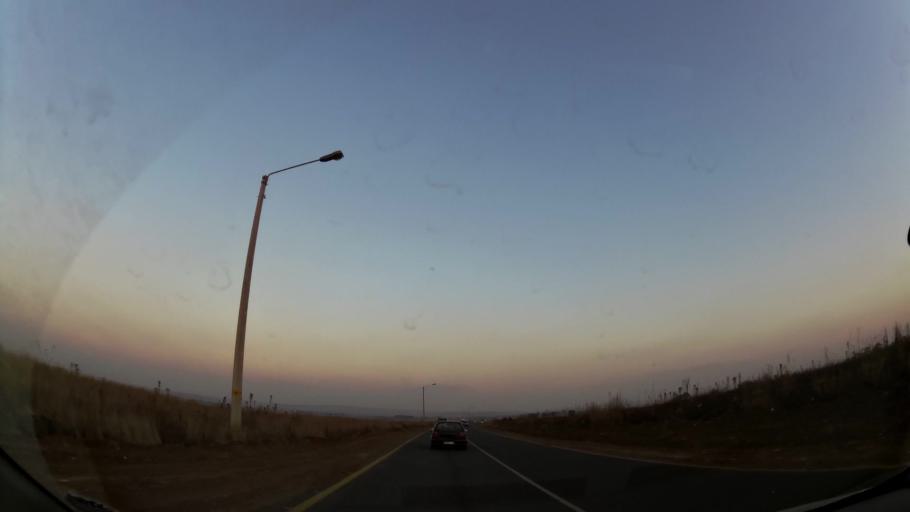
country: ZA
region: Gauteng
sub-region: Ekurhuleni Metropolitan Municipality
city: Nigel
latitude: -26.3667
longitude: 28.4199
